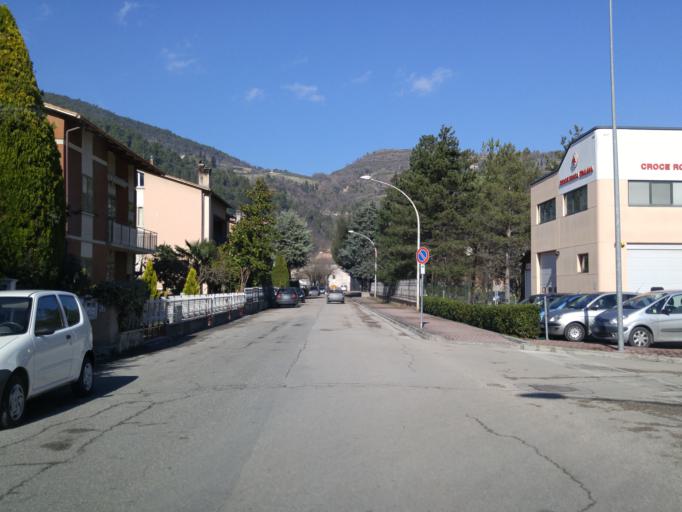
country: IT
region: The Marches
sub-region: Provincia di Pesaro e Urbino
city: Fossombrone
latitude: 43.6844
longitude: 12.8039
